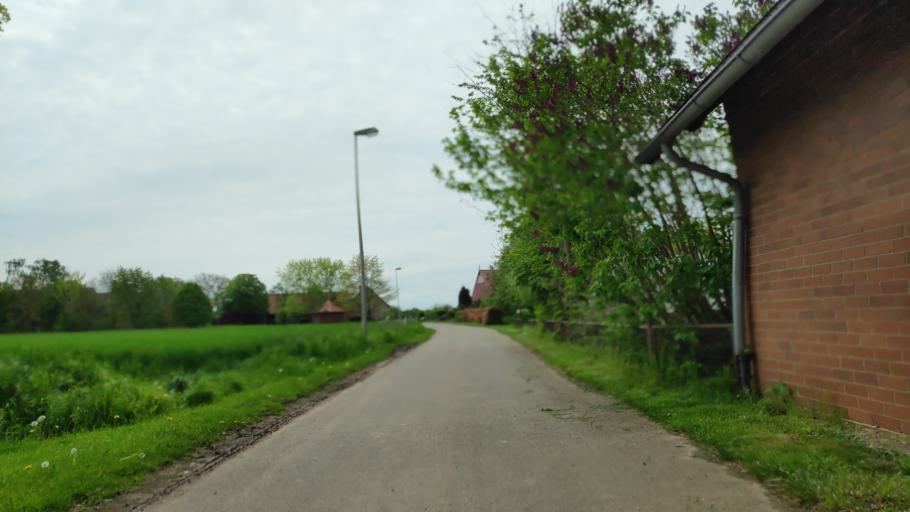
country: DE
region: North Rhine-Westphalia
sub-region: Regierungsbezirk Detmold
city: Petershagen
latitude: 52.3159
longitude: 8.9937
